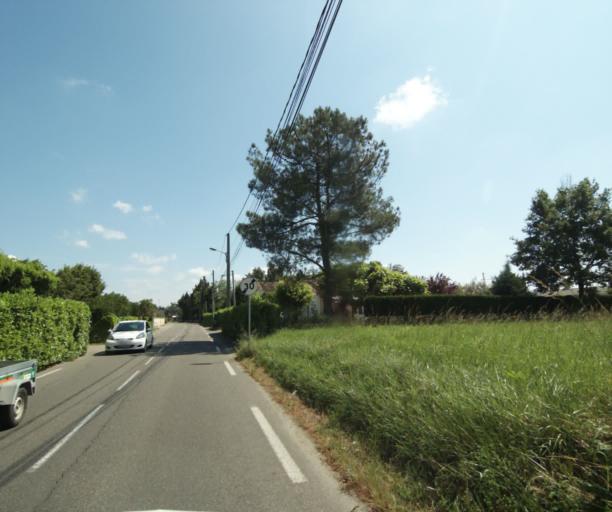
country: FR
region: Midi-Pyrenees
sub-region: Departement du Tarn-et-Garonne
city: Montauban
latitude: 44.0323
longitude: 1.3459
